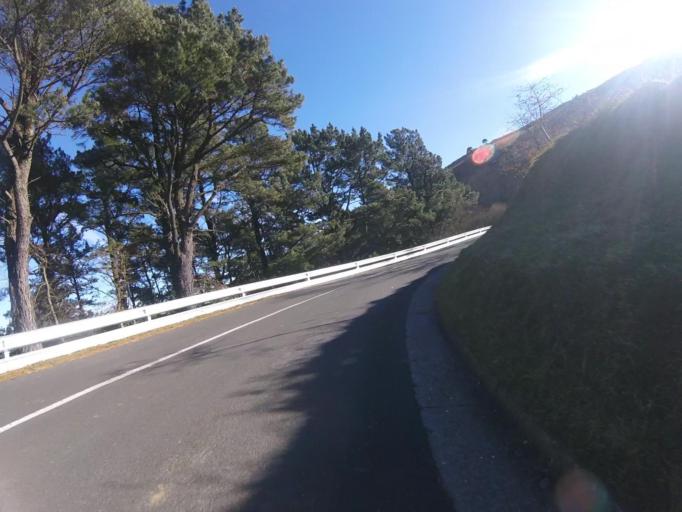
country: ES
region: Basque Country
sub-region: Provincia de Guipuzcoa
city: Lezo
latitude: 43.3476
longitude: -1.8583
